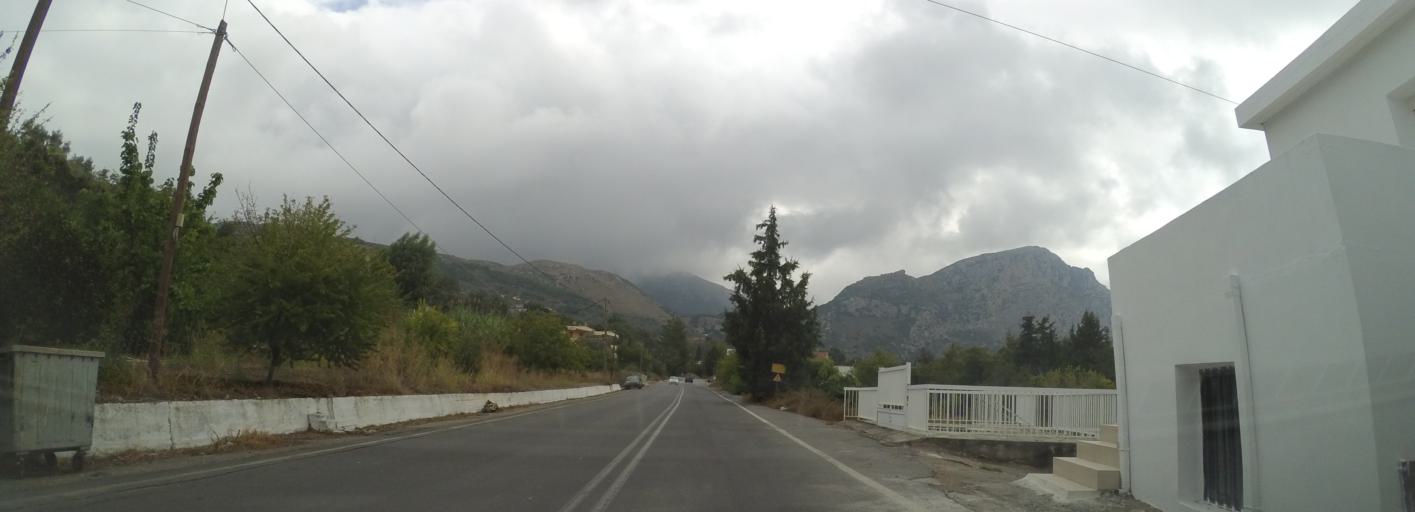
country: GR
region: Crete
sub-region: Nomos Rethymnis
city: Agia Foteini
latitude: 35.2197
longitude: 24.5220
